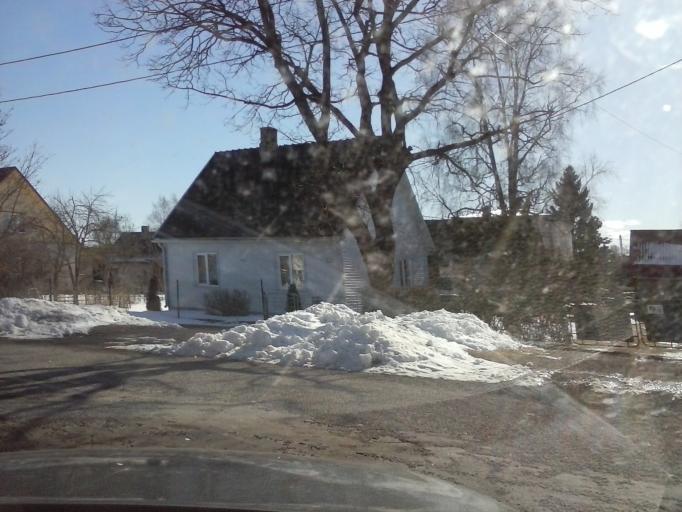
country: EE
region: Jogevamaa
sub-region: Jogeva linn
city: Jogeva
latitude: 58.7436
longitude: 26.3913
